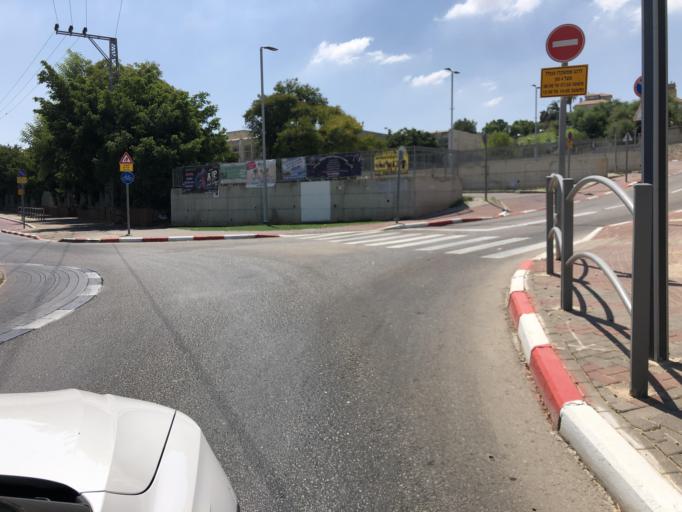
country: IL
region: Central District
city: Rosh Ha'Ayin
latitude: 32.0980
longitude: 34.9585
